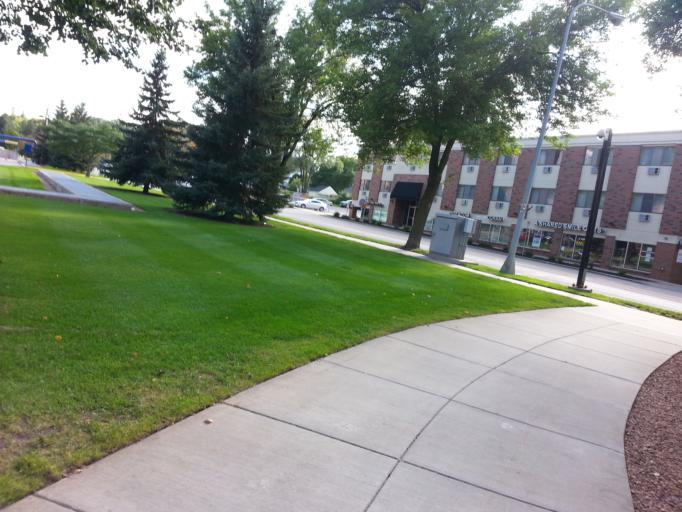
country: US
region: Minnesota
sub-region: Olmsted County
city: Rochester
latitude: 44.0214
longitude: -92.4837
